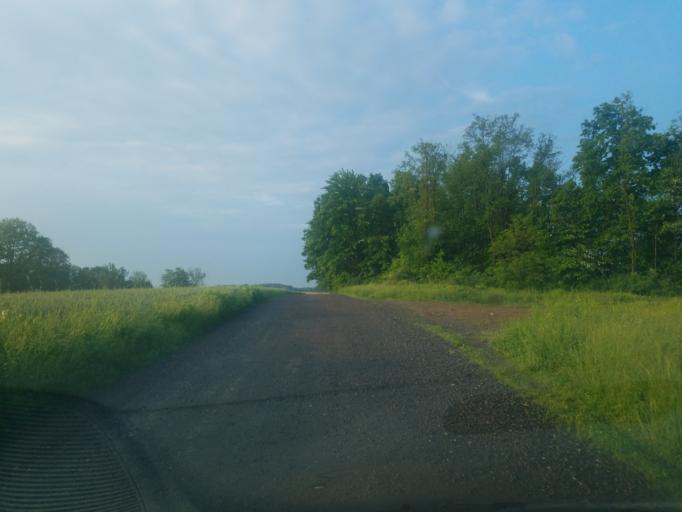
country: US
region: Ohio
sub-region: Stark County
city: Minerva
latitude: 40.7289
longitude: -80.9847
